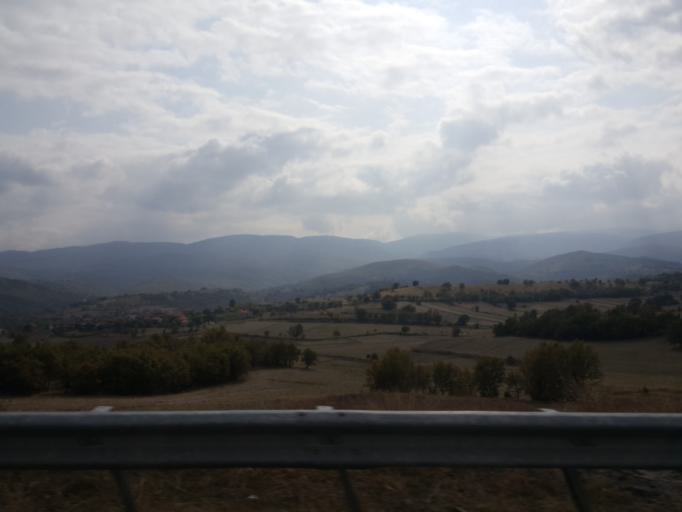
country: TR
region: Sinop
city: Sarayduzu
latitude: 41.3422
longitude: 34.8015
